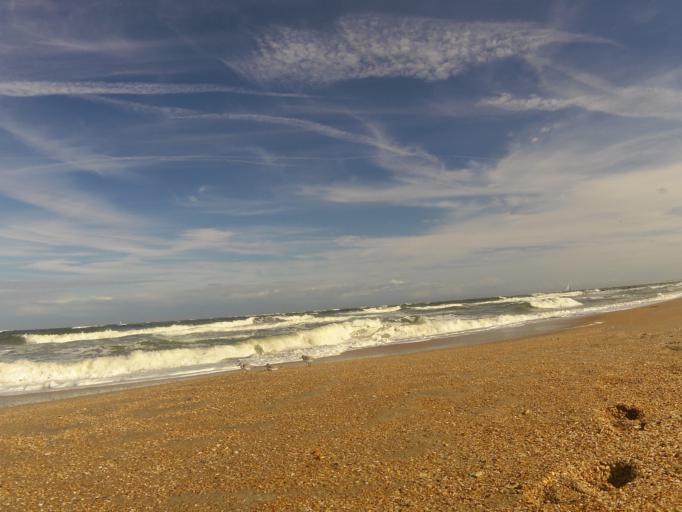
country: US
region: Florida
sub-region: Saint Johns County
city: Villano Beach
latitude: 29.9161
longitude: -81.2896
